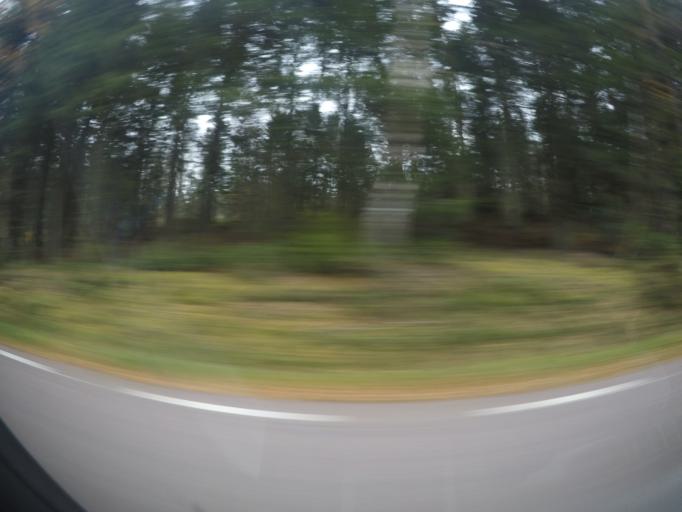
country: SE
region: Vaestmanland
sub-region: Surahammars Kommun
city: Ramnas
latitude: 59.6922
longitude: 16.0819
